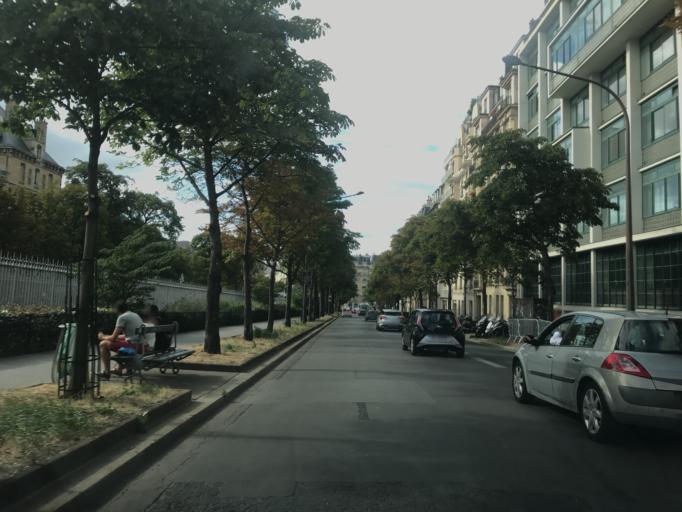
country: FR
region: Ile-de-France
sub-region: Departement des Hauts-de-Seine
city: Malakoff
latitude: 48.8429
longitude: 2.3127
